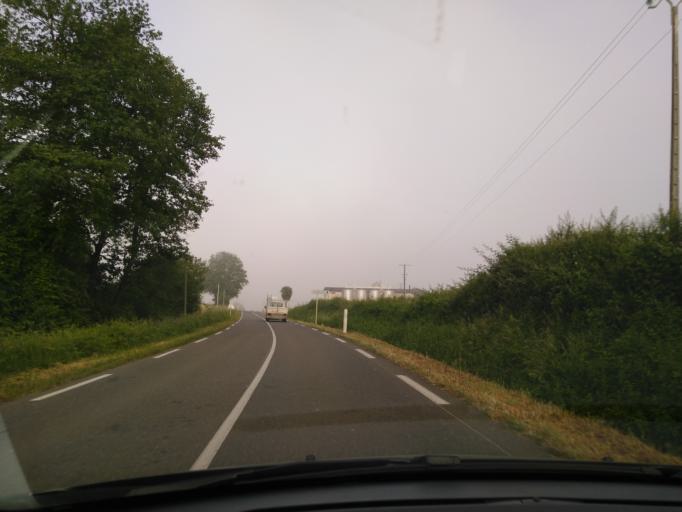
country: FR
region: Midi-Pyrenees
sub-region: Departement du Gers
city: Gondrin
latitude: 43.8783
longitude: 0.1729
